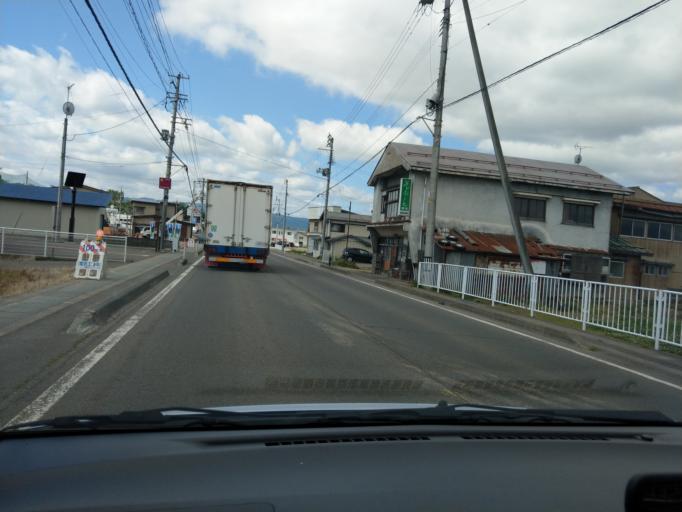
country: JP
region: Akita
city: Yuzawa
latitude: 39.1829
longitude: 140.4974
